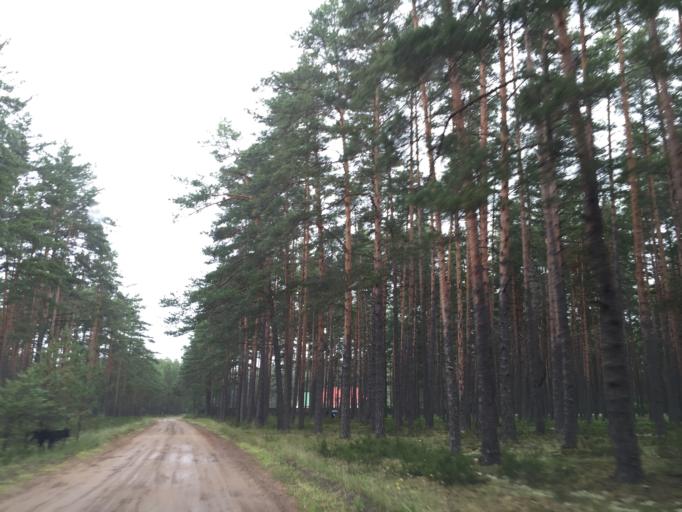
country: LV
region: Riga
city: Jaunciems
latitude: 57.0512
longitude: 24.2057
